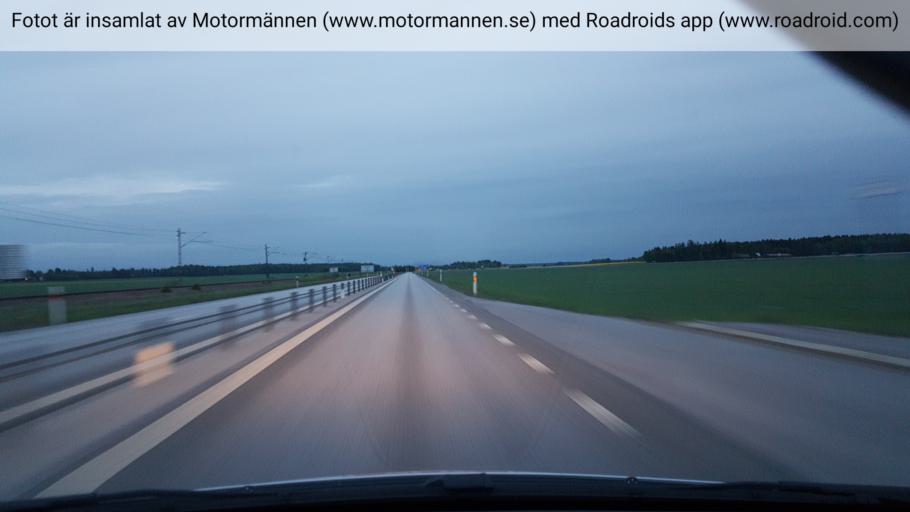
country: SE
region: Vaestmanland
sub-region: Sala Kommun
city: Sala
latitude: 59.8943
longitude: 16.6227
